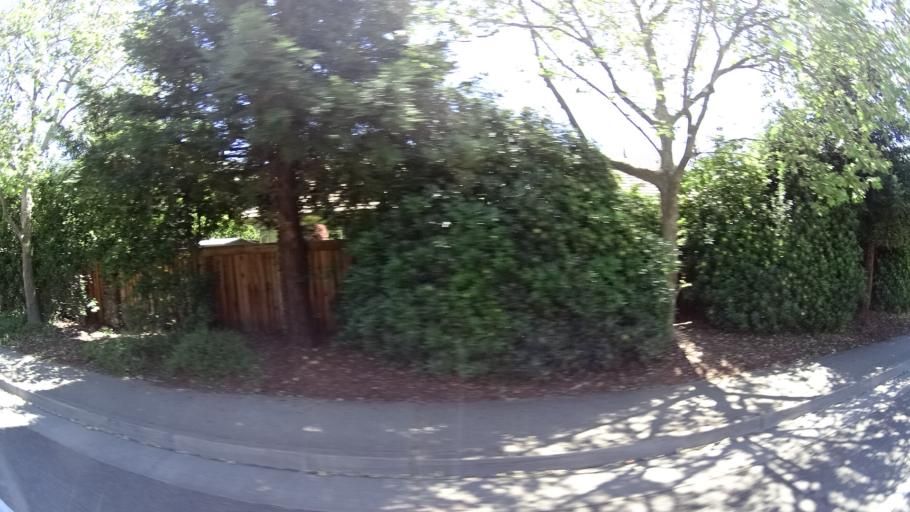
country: US
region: California
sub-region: Placer County
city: Rocklin
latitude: 38.8088
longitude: -121.2472
